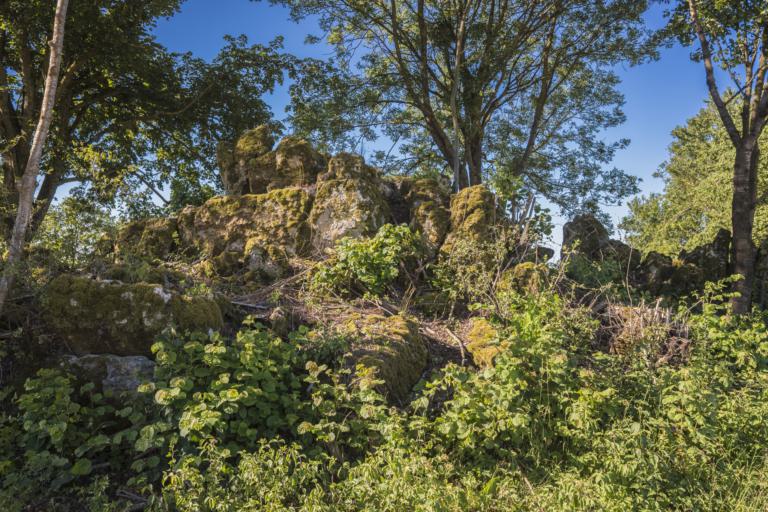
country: DE
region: Bavaria
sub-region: Upper Franconia
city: Poxdorf
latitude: 49.9101
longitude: 11.0961
